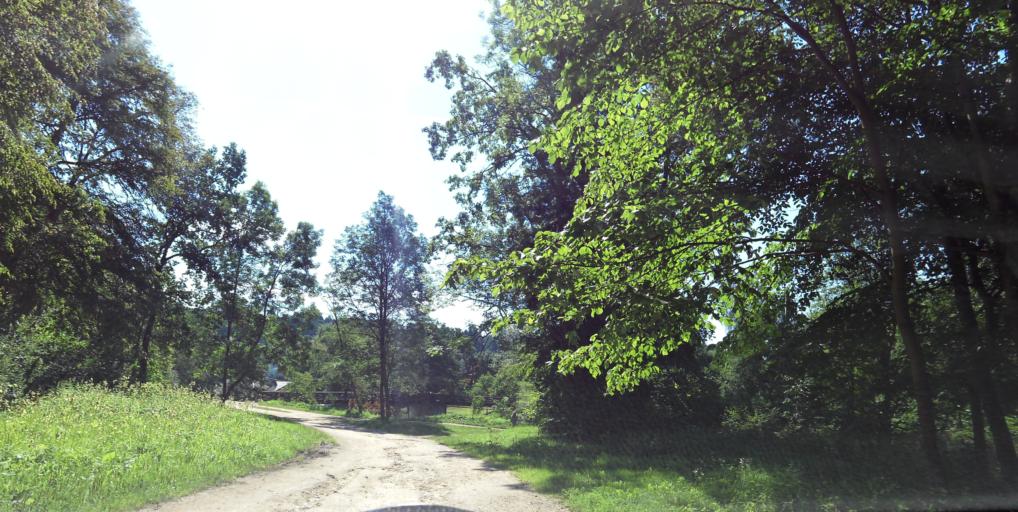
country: LT
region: Vilnius County
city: Rasos
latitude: 54.6861
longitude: 25.3573
